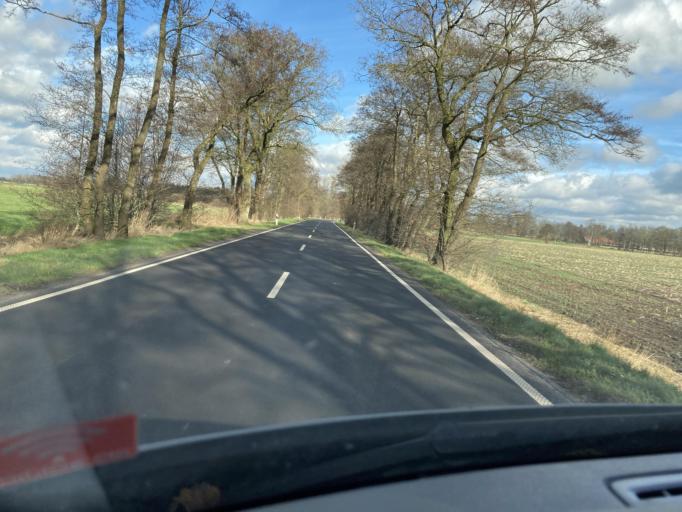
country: DE
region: Lower Saxony
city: Ostrhauderfehn
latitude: 53.1712
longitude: 7.5876
